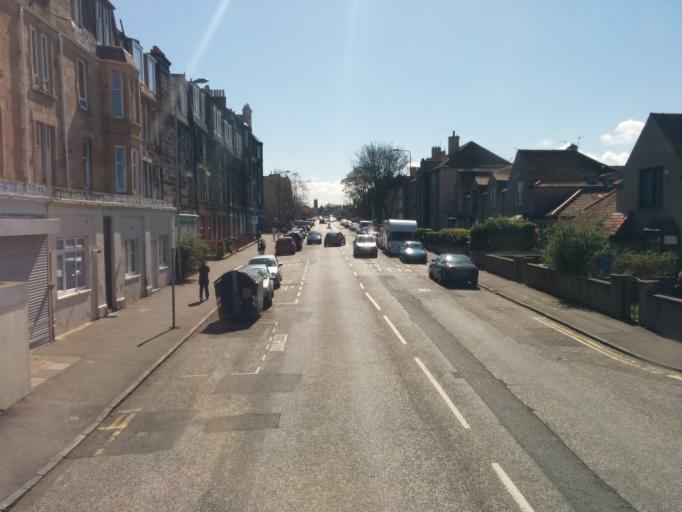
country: GB
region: Scotland
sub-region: Edinburgh
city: Edinburgh
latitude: 55.9773
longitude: -3.2161
